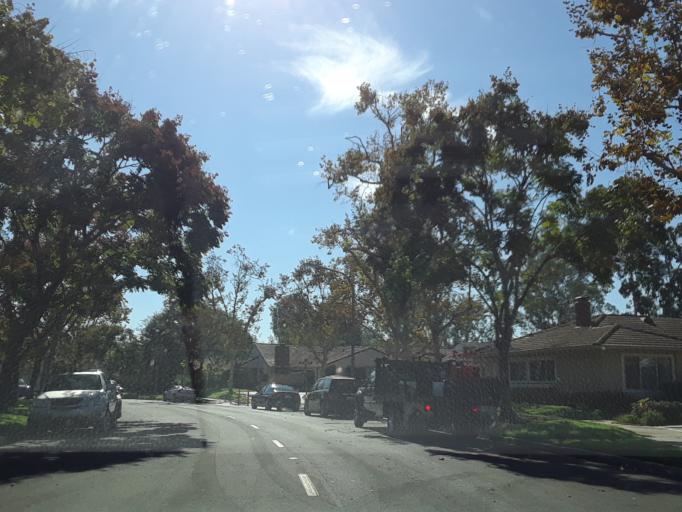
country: US
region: California
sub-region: Orange County
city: Irvine
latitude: 33.6633
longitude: -117.8043
